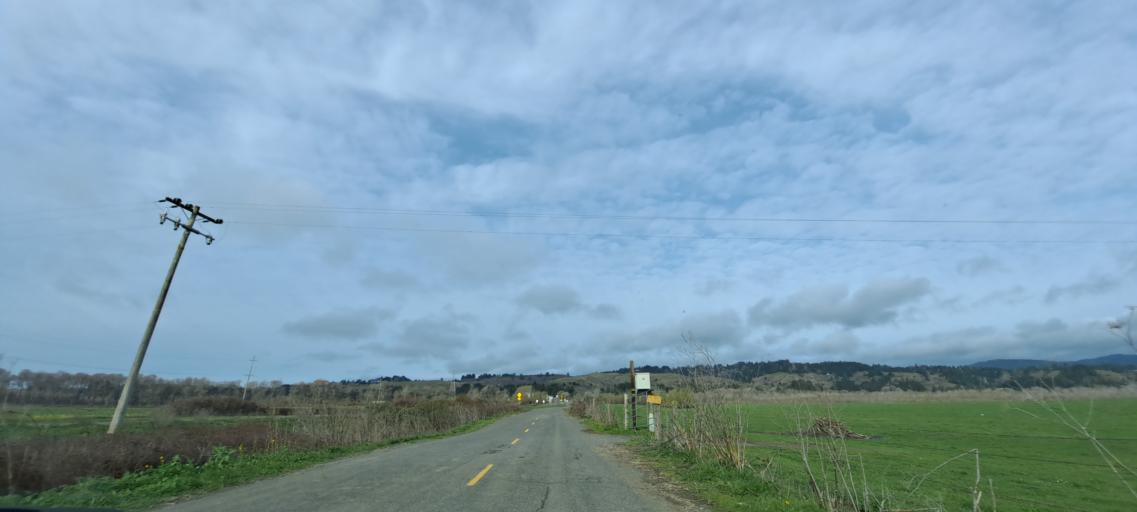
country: US
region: California
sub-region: Humboldt County
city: Fortuna
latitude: 40.6063
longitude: -124.2076
